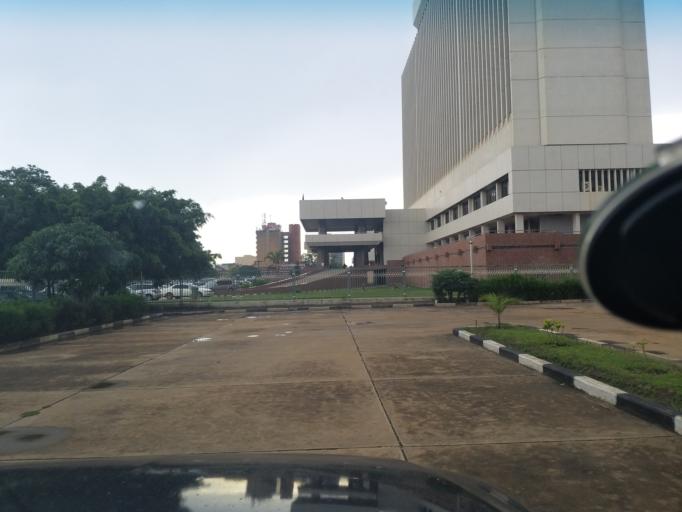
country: ZM
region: Lusaka
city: Lusaka
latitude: -15.4224
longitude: 28.2913
